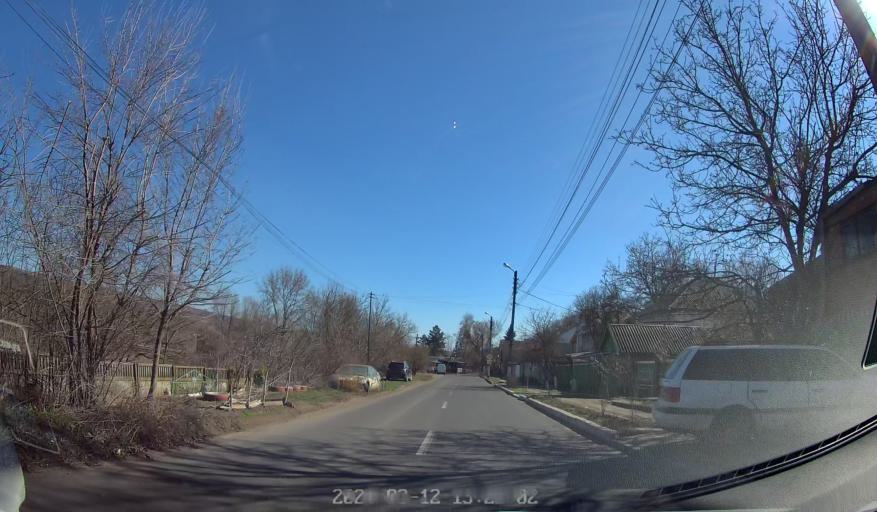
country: MD
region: Laloveni
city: Ialoveni
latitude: 46.9484
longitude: 28.8355
